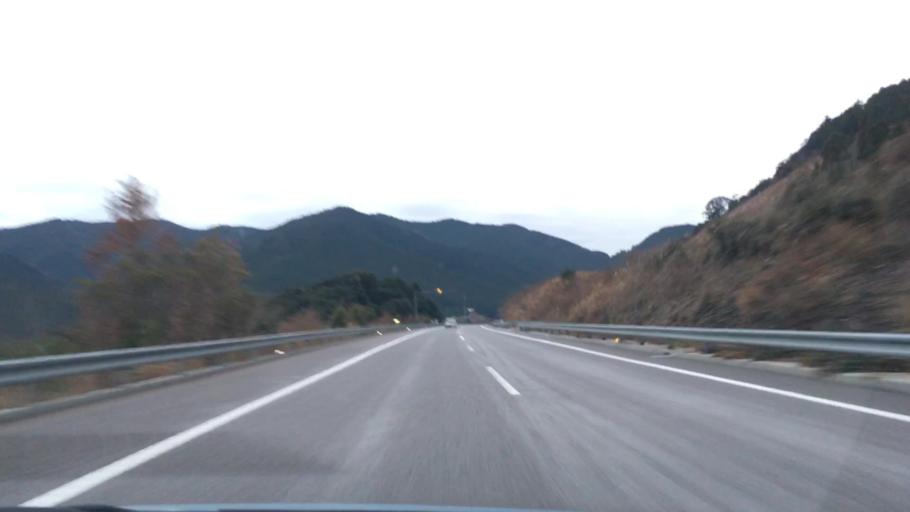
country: JP
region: Aichi
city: Shinshiro
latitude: 34.8444
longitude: 137.6083
